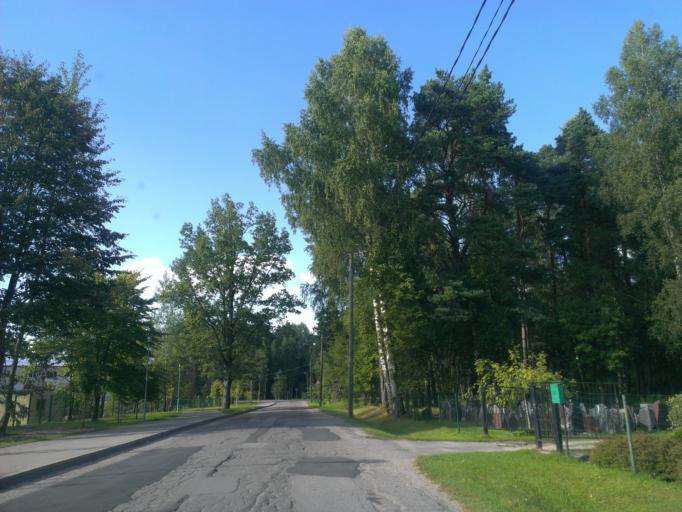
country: LV
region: Sigulda
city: Sigulda
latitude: 57.1690
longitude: 24.8613
